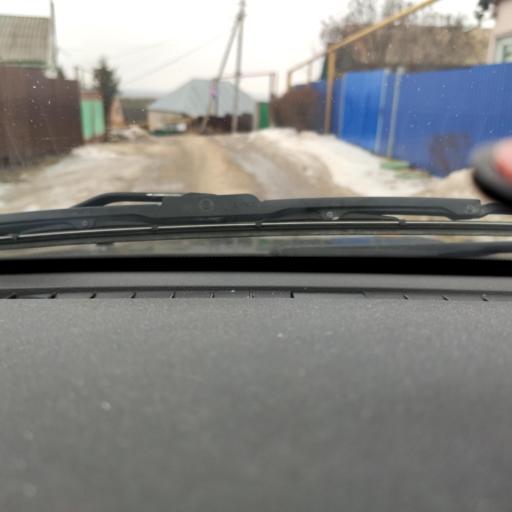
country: RU
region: Voronezj
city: Ramon'
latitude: 51.8177
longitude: 39.2719
